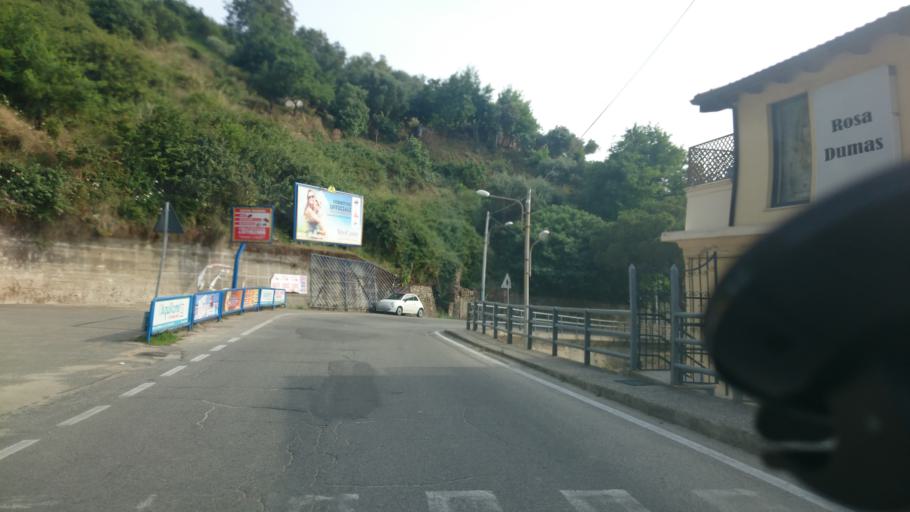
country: IT
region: Calabria
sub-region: Provincia di Vibo-Valentia
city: Maierato
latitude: 38.7339
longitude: 16.1597
